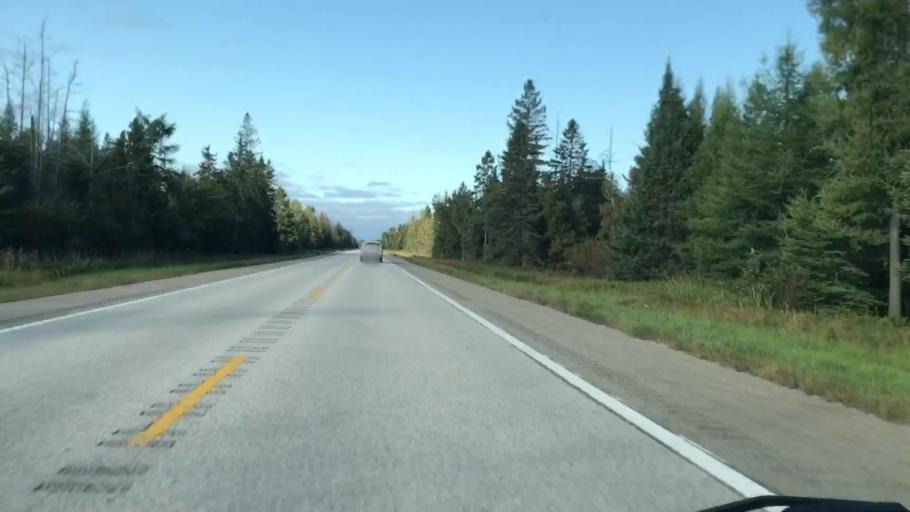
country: US
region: Michigan
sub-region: Luce County
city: Newberry
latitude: 46.3261
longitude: -85.1668
